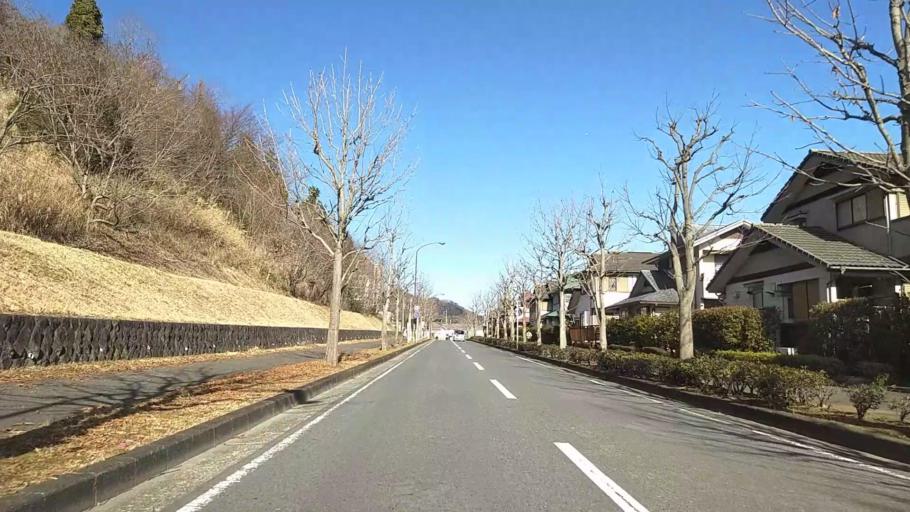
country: JP
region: Kanagawa
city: Atsugi
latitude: 35.4498
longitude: 139.3038
